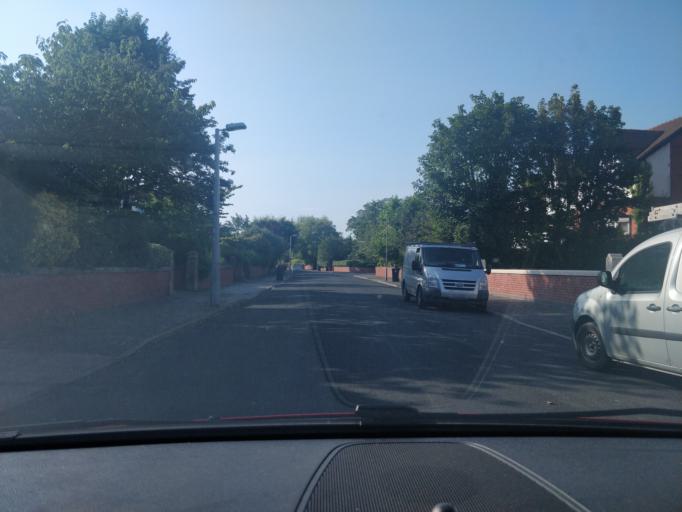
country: GB
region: England
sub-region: Sefton
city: Southport
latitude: 53.6561
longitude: -2.9804
